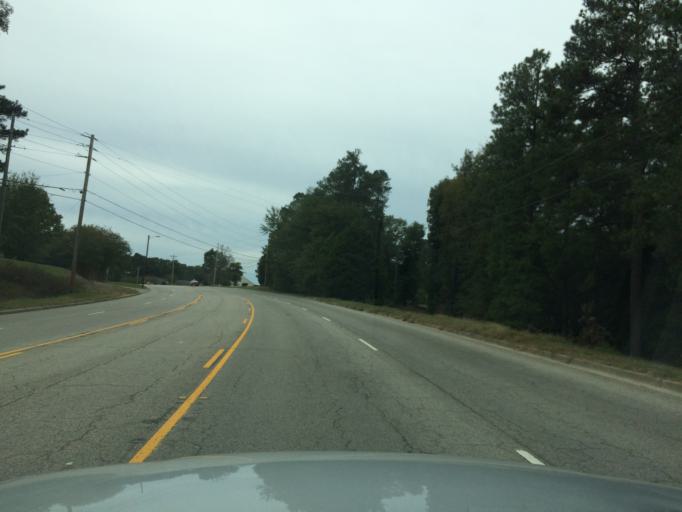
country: US
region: South Carolina
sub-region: Aiken County
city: Aiken
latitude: 33.5864
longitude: -81.6991
